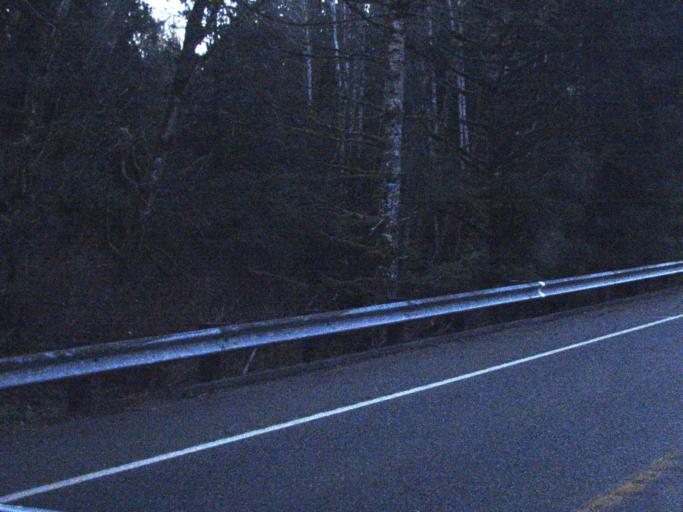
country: US
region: Washington
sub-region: Snohomish County
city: Darrington
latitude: 48.5006
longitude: -121.6479
